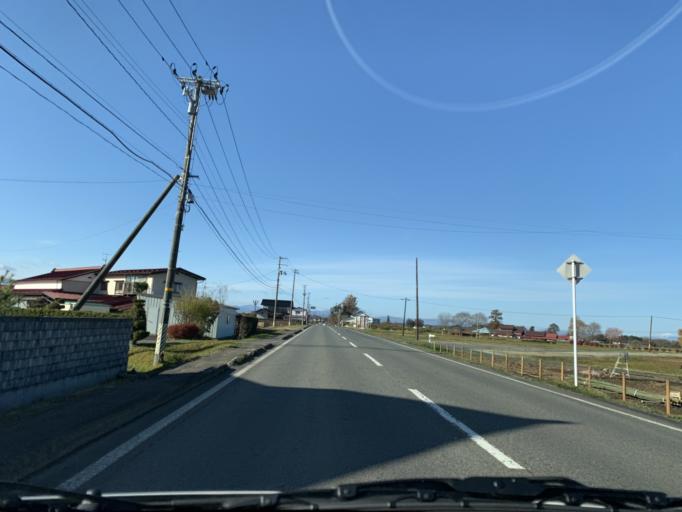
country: JP
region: Iwate
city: Mizusawa
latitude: 39.1773
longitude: 141.1365
